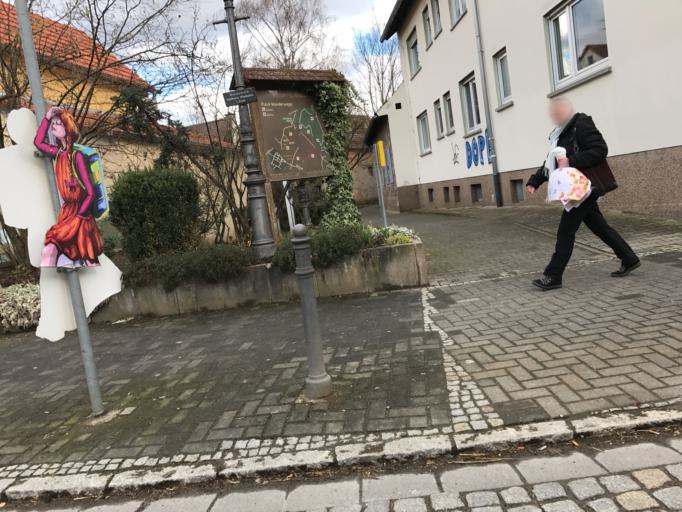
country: DE
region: Hesse
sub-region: Regierungsbezirk Darmstadt
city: Niedernhausen
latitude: 50.0944
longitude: 8.3065
